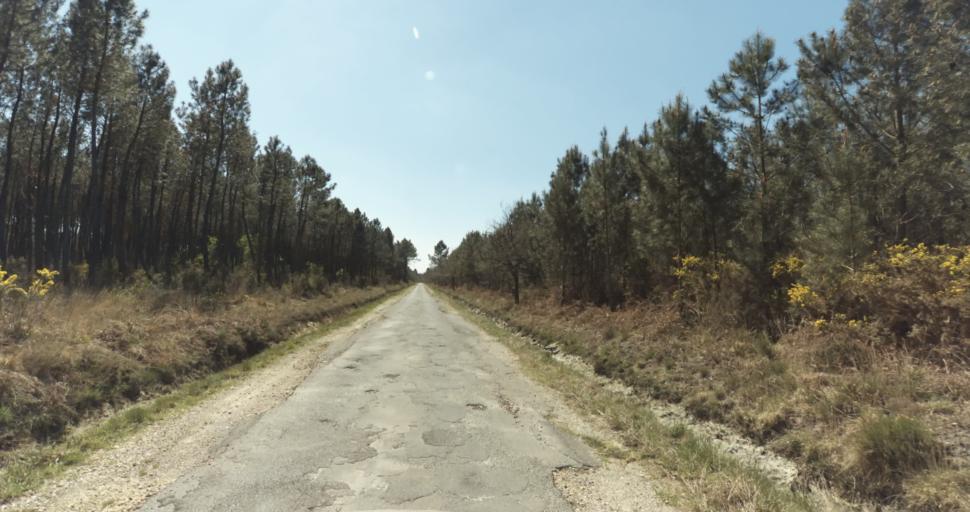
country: FR
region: Aquitaine
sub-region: Departement de la Gironde
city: Martignas-sur-Jalle
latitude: 44.7955
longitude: -0.7549
